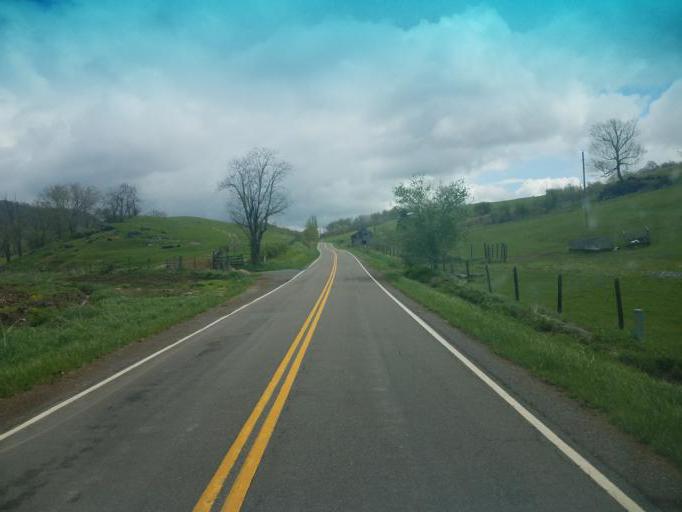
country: US
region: Virginia
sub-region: Smyth County
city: Atkins
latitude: 37.0010
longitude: -81.3747
